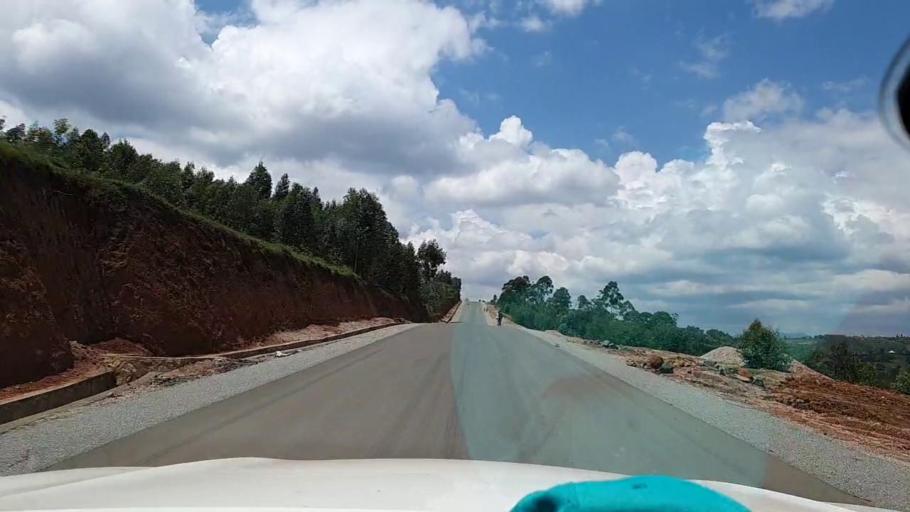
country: RW
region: Southern Province
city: Nzega
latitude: -2.6424
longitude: 29.5757
